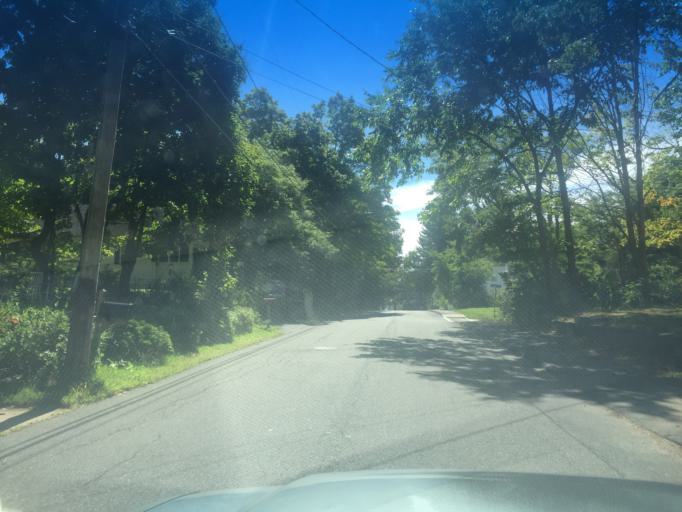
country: US
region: Massachusetts
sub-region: Norfolk County
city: Medway
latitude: 42.1422
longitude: -71.4286
